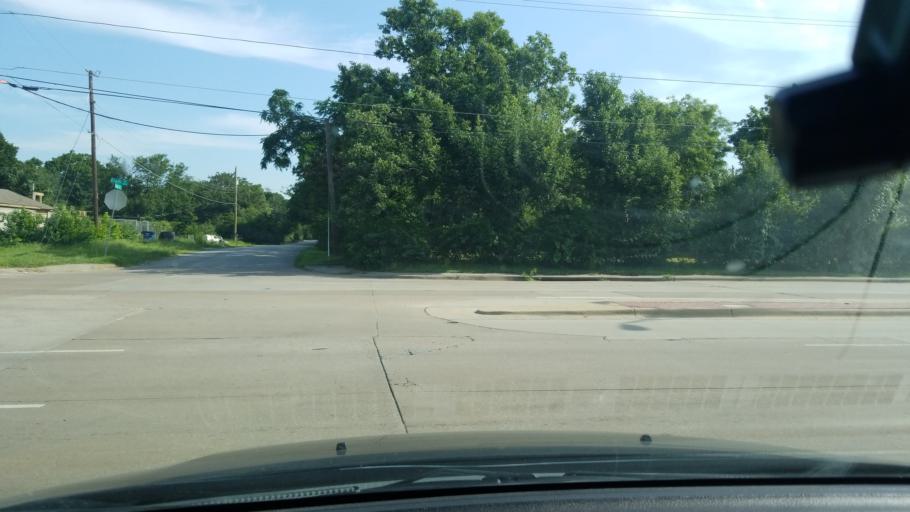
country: US
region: Texas
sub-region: Dallas County
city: Balch Springs
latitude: 32.7194
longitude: -96.6455
